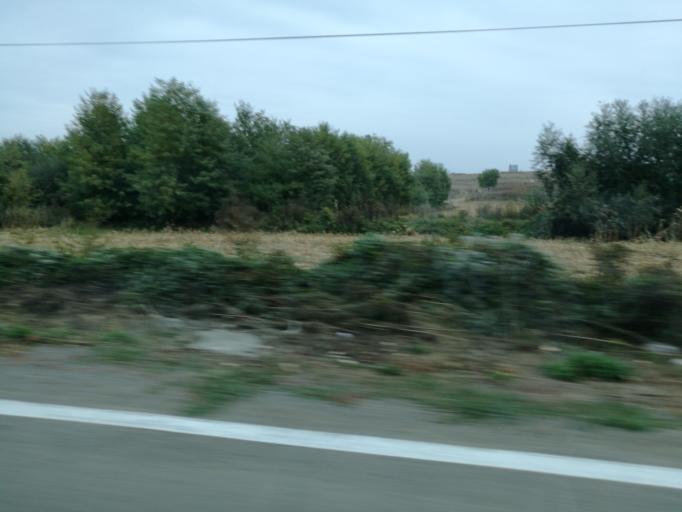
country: RO
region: Tulcea
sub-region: Comuna Ciucurova
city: Ciucurova
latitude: 44.9264
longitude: 28.4482
